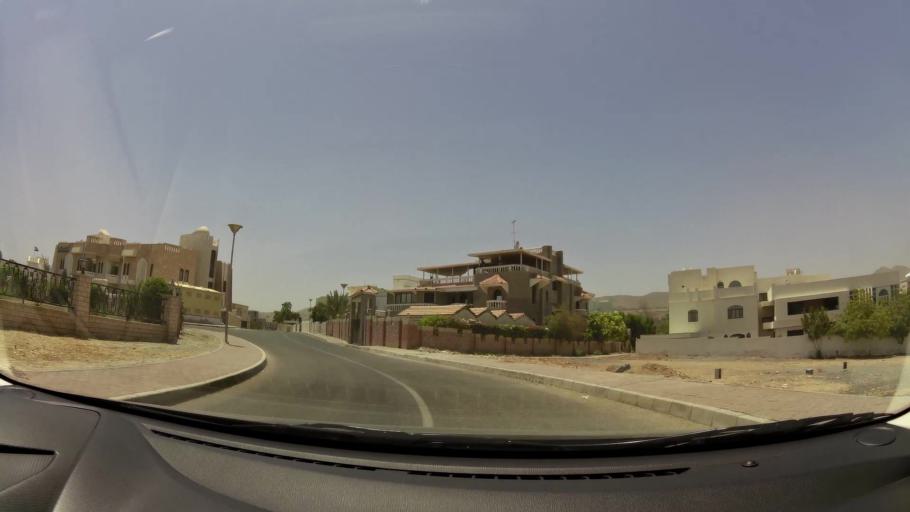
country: OM
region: Muhafazat Masqat
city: Bawshar
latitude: 23.6065
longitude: 58.4731
